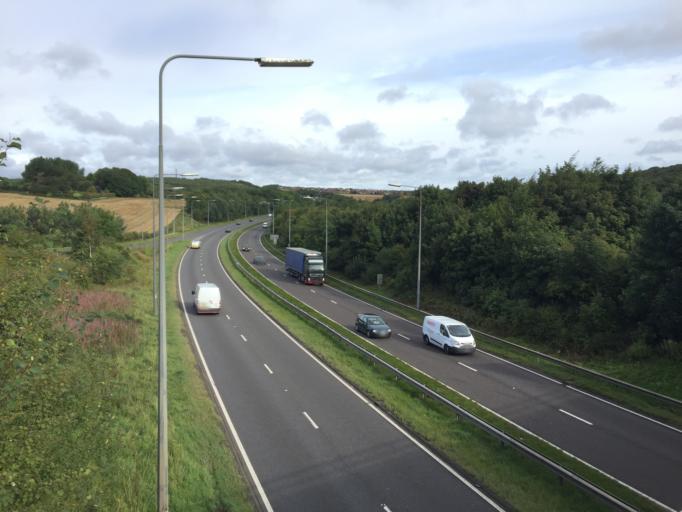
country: GB
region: England
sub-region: County Durham
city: Hawthorn
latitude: 54.8173
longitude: -1.3681
